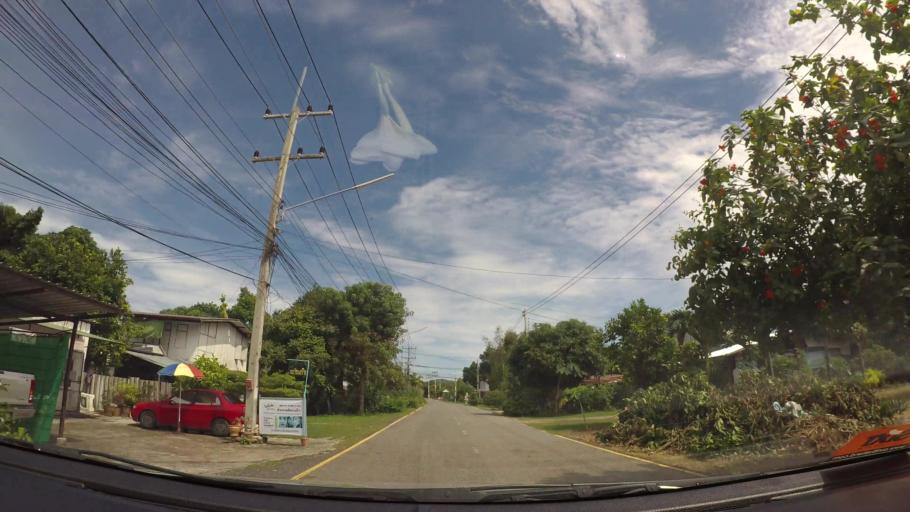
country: TH
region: Chon Buri
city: Sattahip
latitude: 12.6667
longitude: 100.9115
